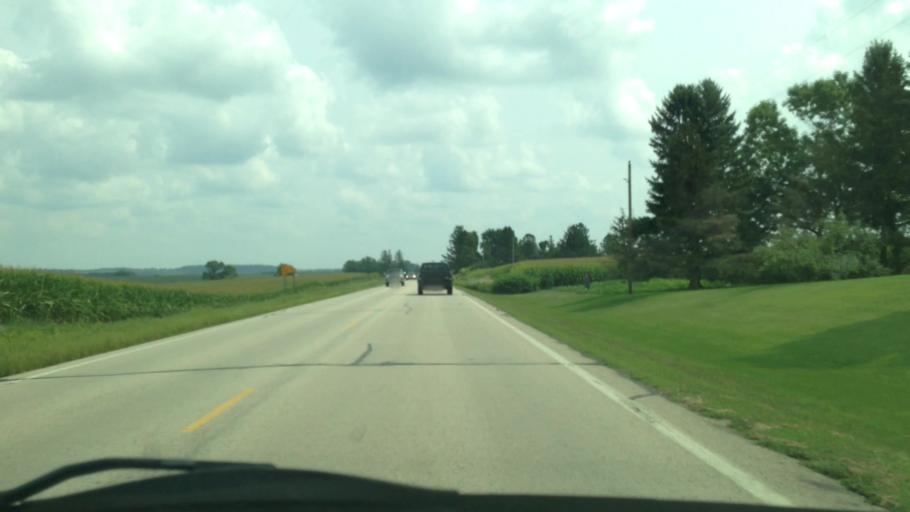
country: US
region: Minnesota
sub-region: Wabasha County
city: Elgin
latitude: 44.1368
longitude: -92.3526
